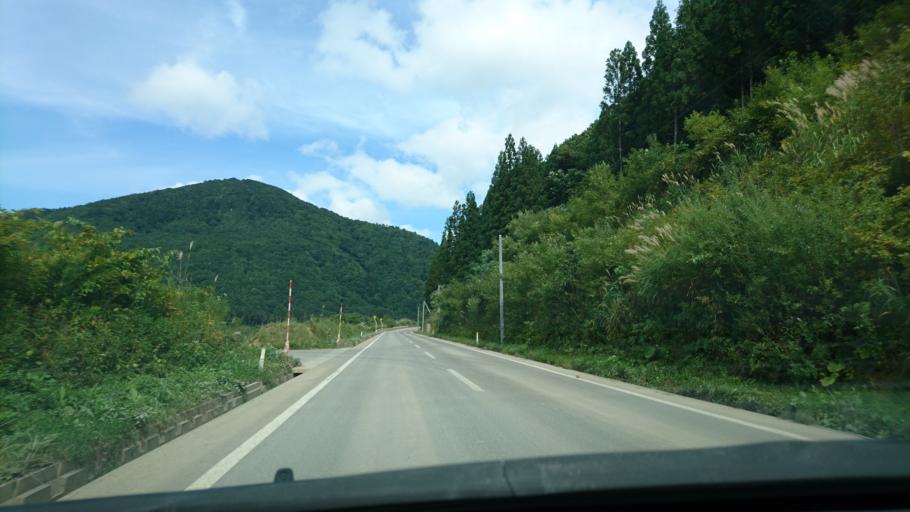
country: JP
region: Akita
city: Yuzawa
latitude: 39.0326
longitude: 140.7291
